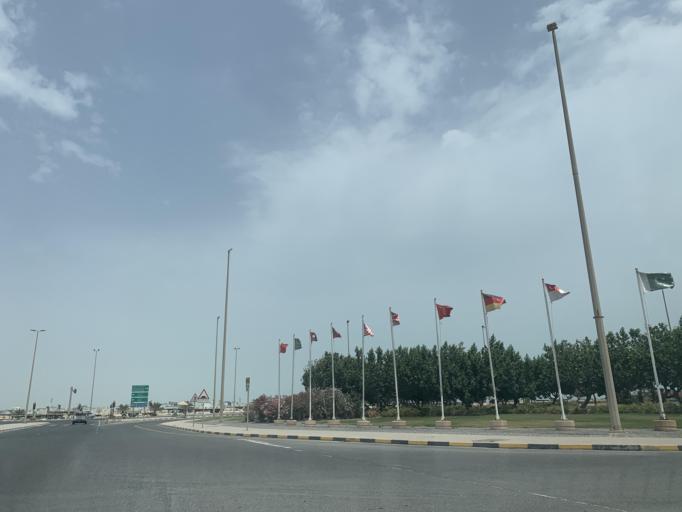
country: BH
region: Muharraq
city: Al Hadd
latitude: 26.2240
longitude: 50.6742
